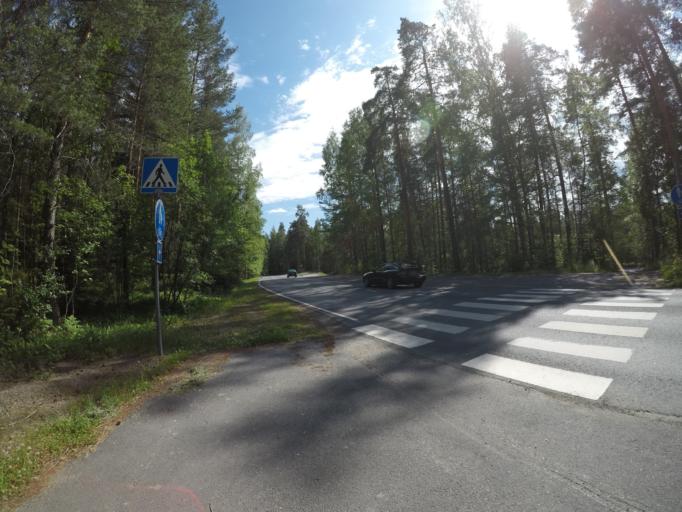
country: FI
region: Haeme
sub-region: Haemeenlinna
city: Haemeenlinna
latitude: 60.9936
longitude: 24.4049
